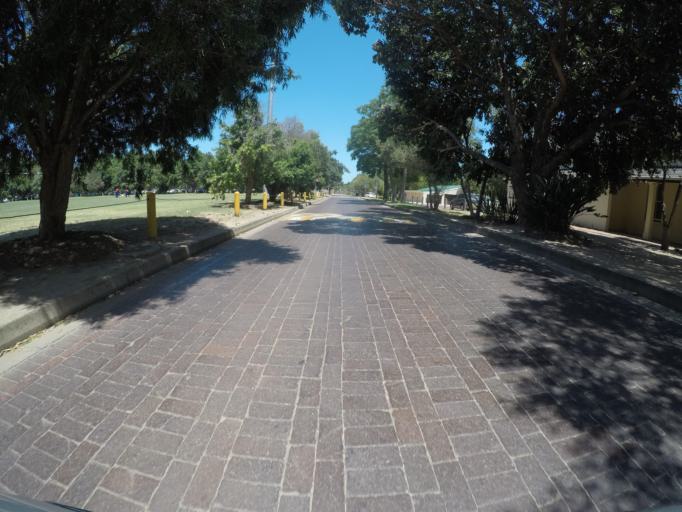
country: ZA
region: Western Cape
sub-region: Cape Winelands District Municipality
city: Stellenbosch
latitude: -33.9385
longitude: 18.8715
